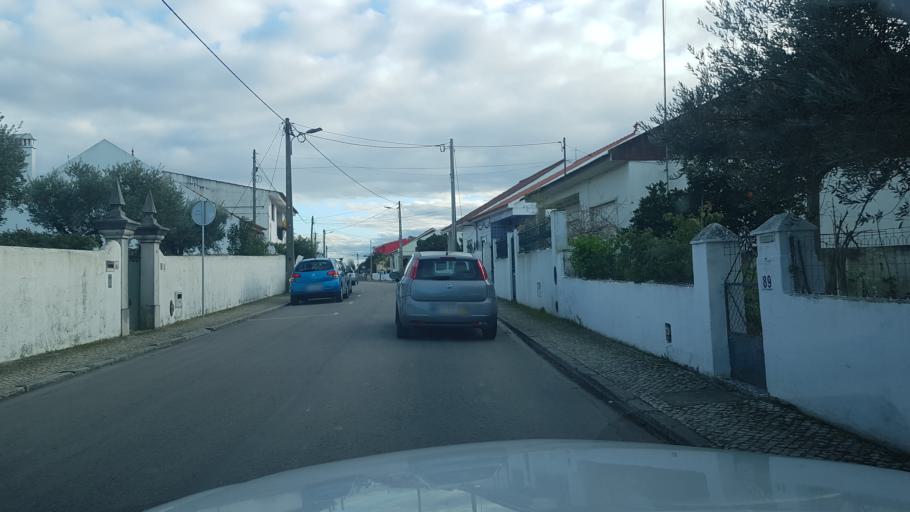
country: PT
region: Santarem
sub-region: Entroncamento
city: Entroncamento
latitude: 39.4767
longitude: -8.4809
